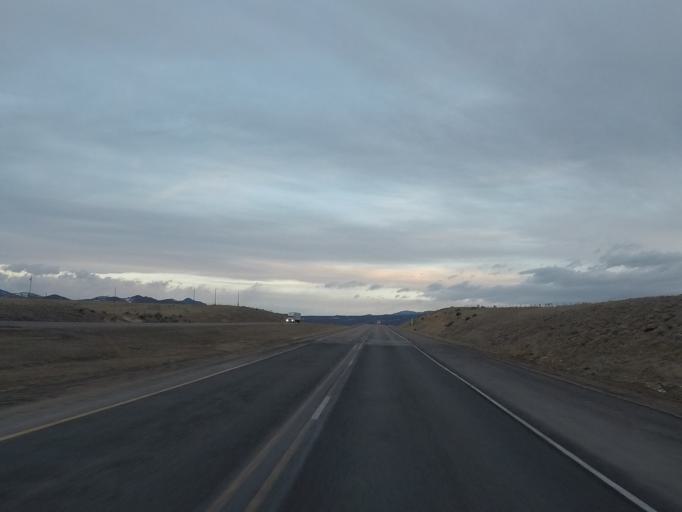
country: US
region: Montana
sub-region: Jefferson County
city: Whitehall
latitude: 45.8937
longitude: -112.1799
